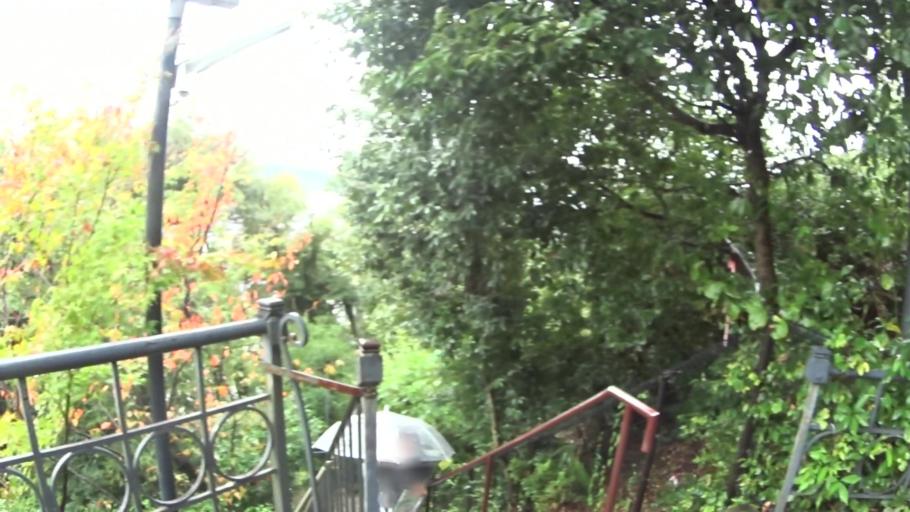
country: JP
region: Shiga Prefecture
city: Otsu-shi
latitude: 34.9858
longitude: 135.8083
